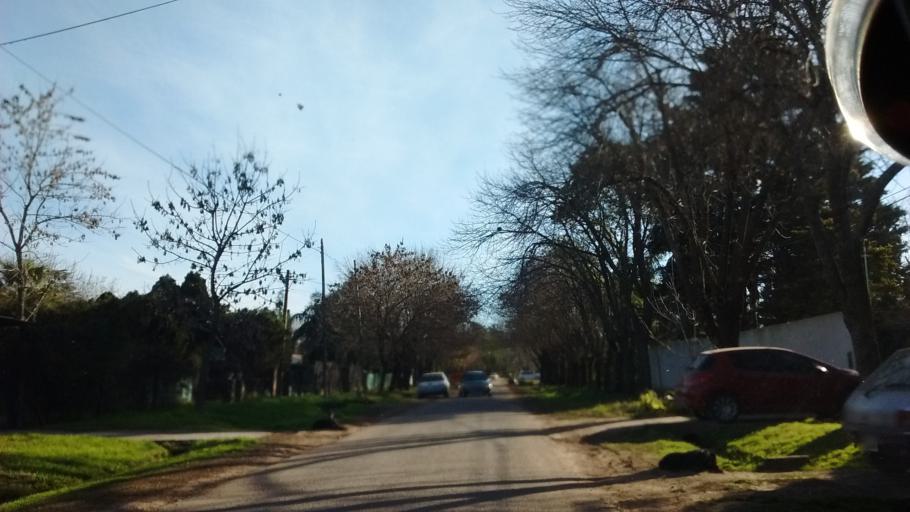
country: AR
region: Santa Fe
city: Funes
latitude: -32.9260
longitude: -60.8069
